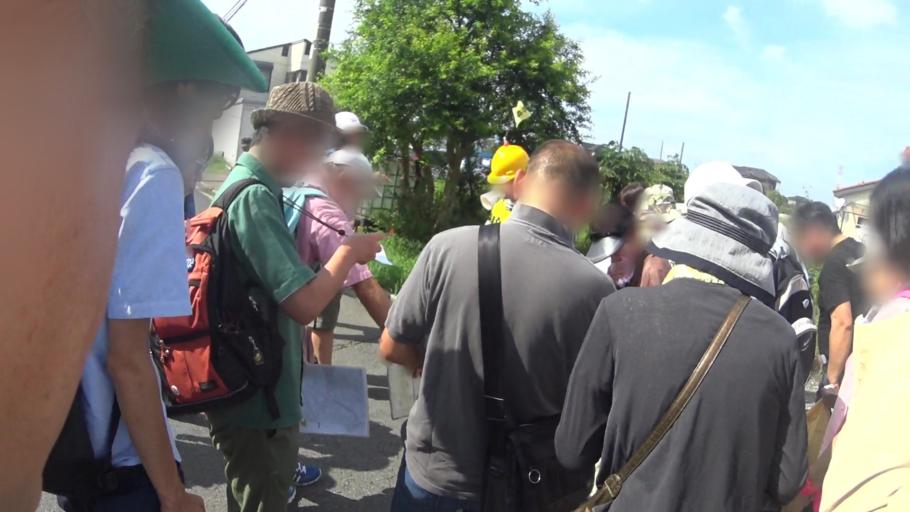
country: JP
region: Saitama
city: Kasukabe
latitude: 35.9695
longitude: 139.7204
